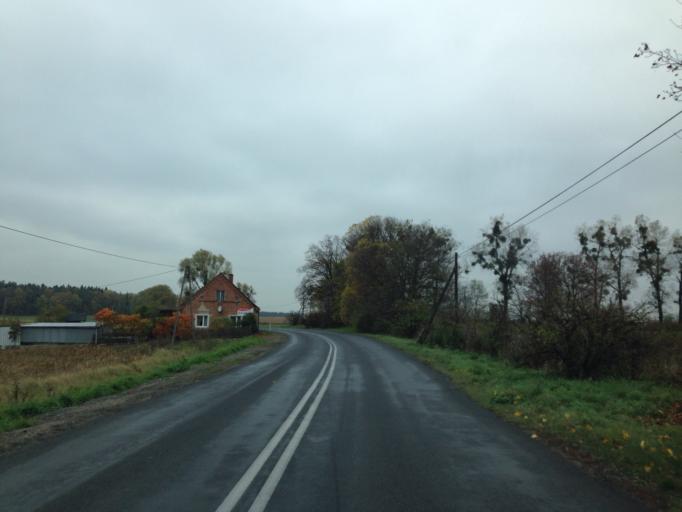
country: PL
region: Kujawsko-Pomorskie
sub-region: Powiat brodnicki
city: Bobrowo
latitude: 53.3171
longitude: 19.2759
